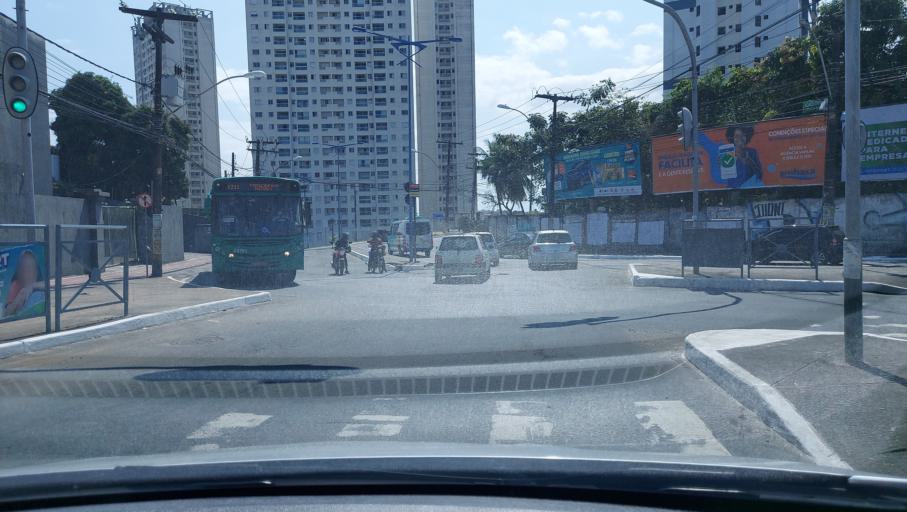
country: BR
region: Bahia
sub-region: Salvador
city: Salvador
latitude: -12.9656
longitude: -38.4726
